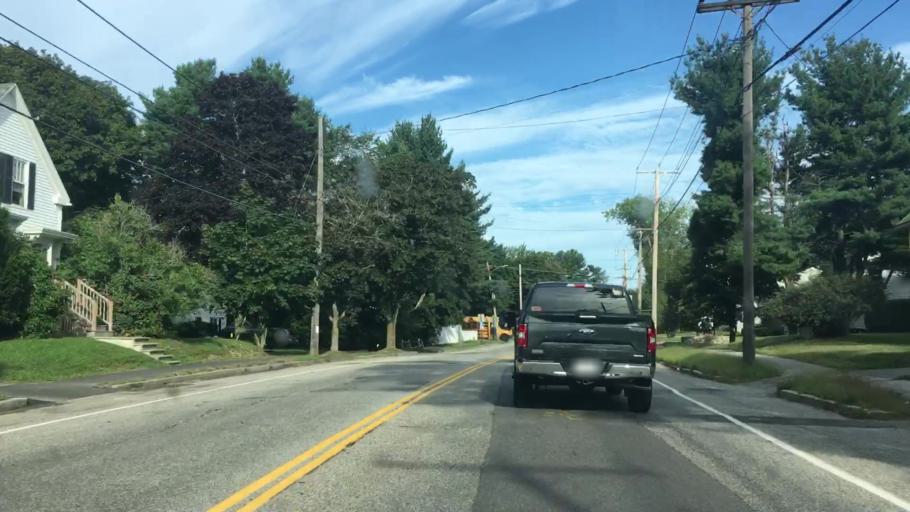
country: US
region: Maine
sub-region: Cumberland County
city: Portland
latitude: 43.6921
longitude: -70.2808
